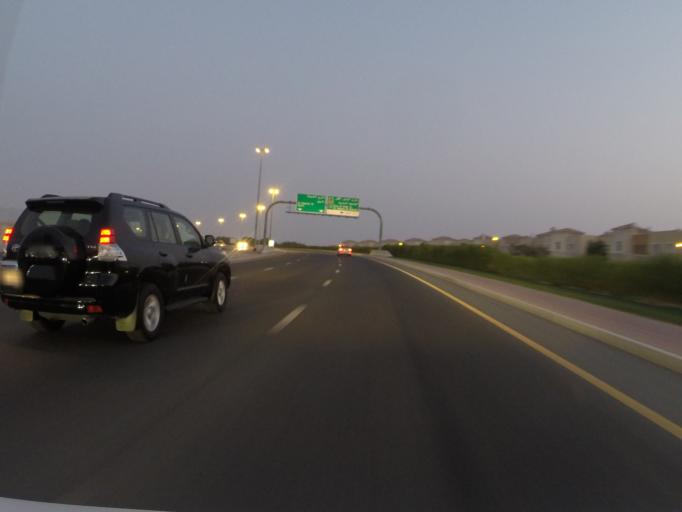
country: AE
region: Dubai
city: Dubai
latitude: 25.0834
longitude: 55.1727
